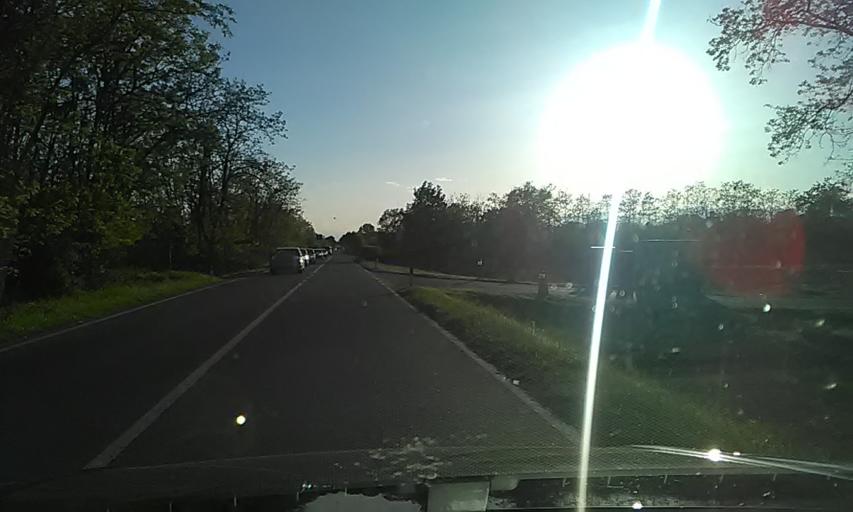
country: IT
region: Piedmont
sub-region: Provincia di Novara
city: Carpignano Sesia
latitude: 45.5310
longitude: 8.4021
